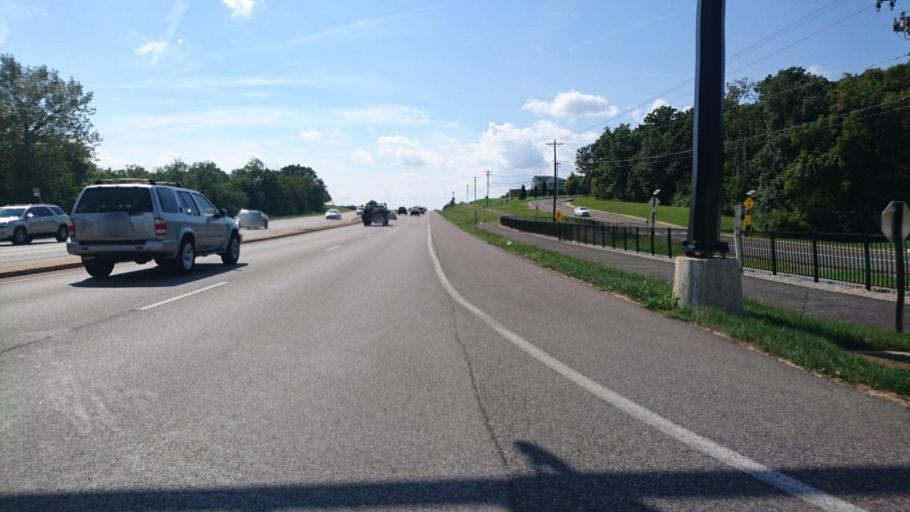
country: US
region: Missouri
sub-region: Saint Louis County
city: Ellisville
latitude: 38.5898
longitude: -90.5989
